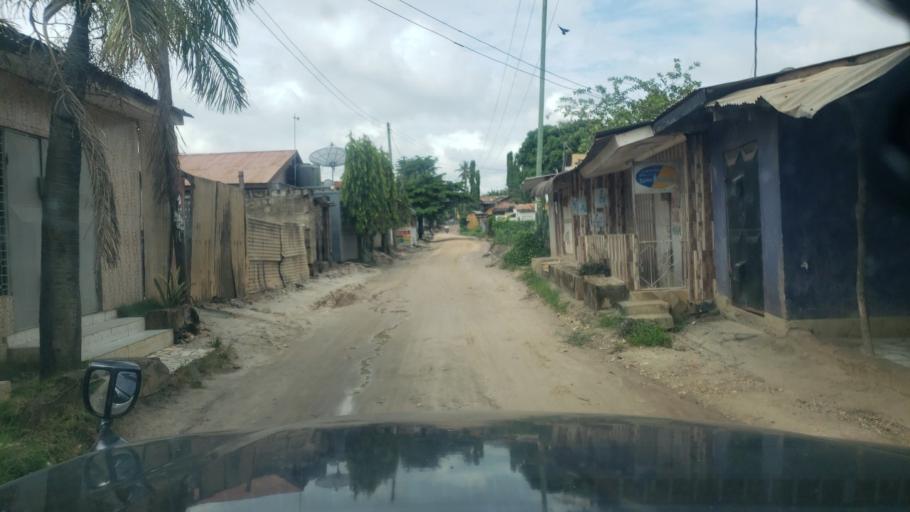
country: TZ
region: Pwani
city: Vikindu
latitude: -6.9196
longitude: 39.2564
